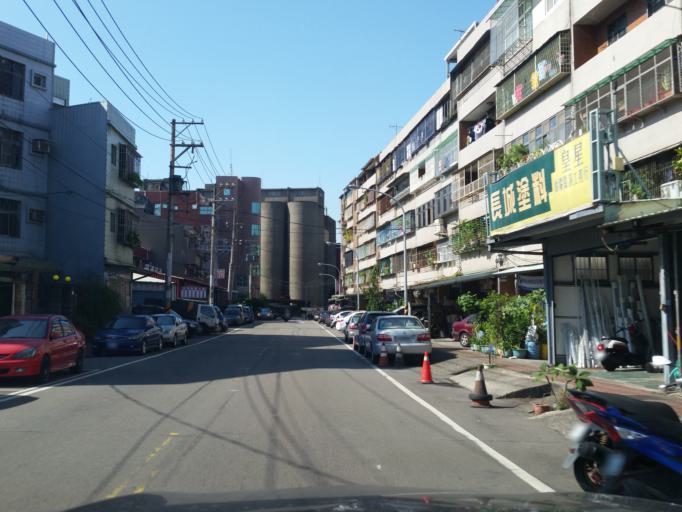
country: TW
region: Taiwan
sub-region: Taoyuan
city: Taoyuan
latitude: 24.9877
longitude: 121.3202
